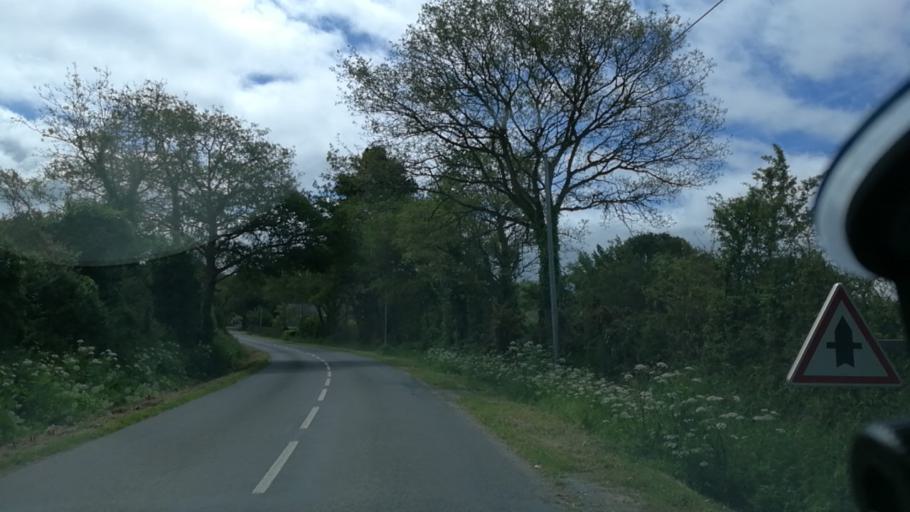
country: FR
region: Pays de la Loire
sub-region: Departement de la Loire-Atlantique
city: Asserac
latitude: 47.4613
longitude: -2.4247
